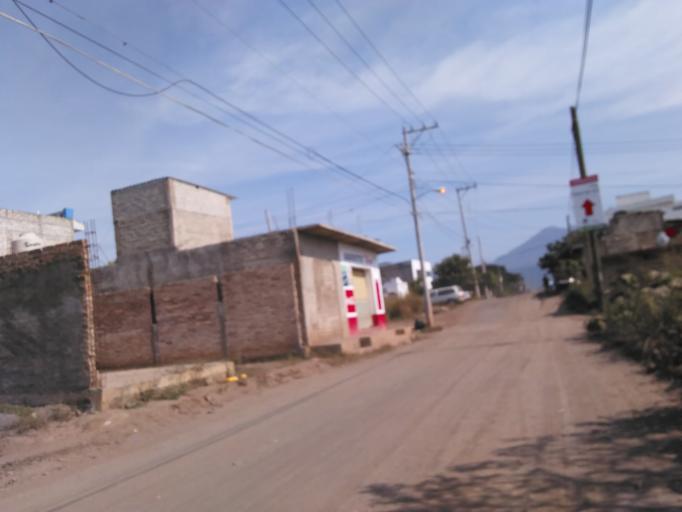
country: MX
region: Nayarit
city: Tepic
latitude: 21.4901
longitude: -104.8496
